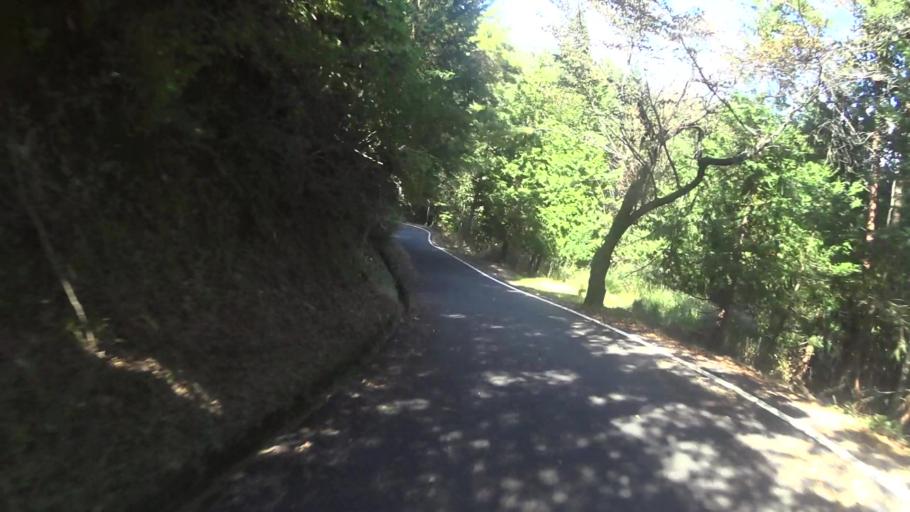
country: JP
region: Hyogo
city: Toyooka
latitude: 35.5420
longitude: 134.9651
